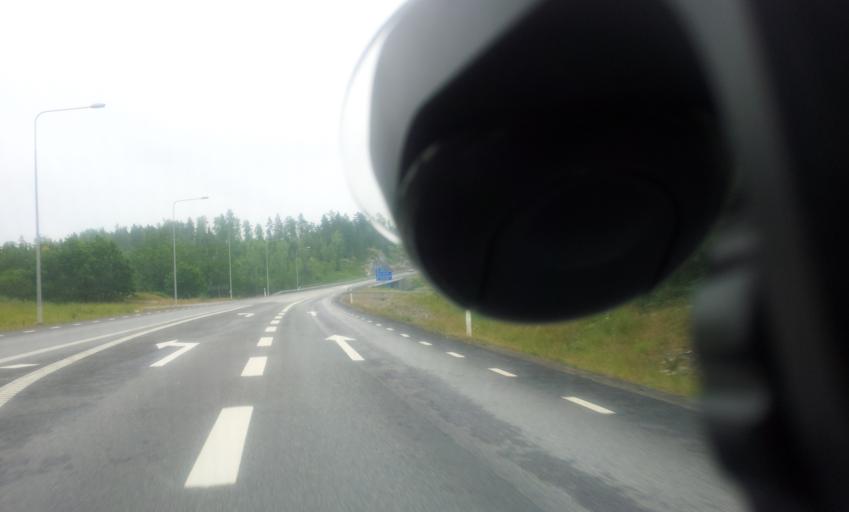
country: SE
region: Kalmar
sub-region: Vasterviks Kommun
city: Ankarsrum
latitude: 57.6629
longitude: 16.4439
